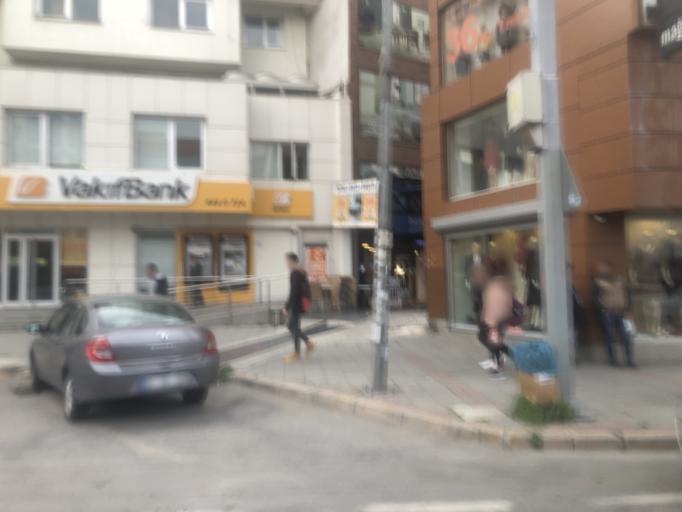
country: TR
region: Izmir
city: Karsiyaka
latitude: 38.4911
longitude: 27.0670
